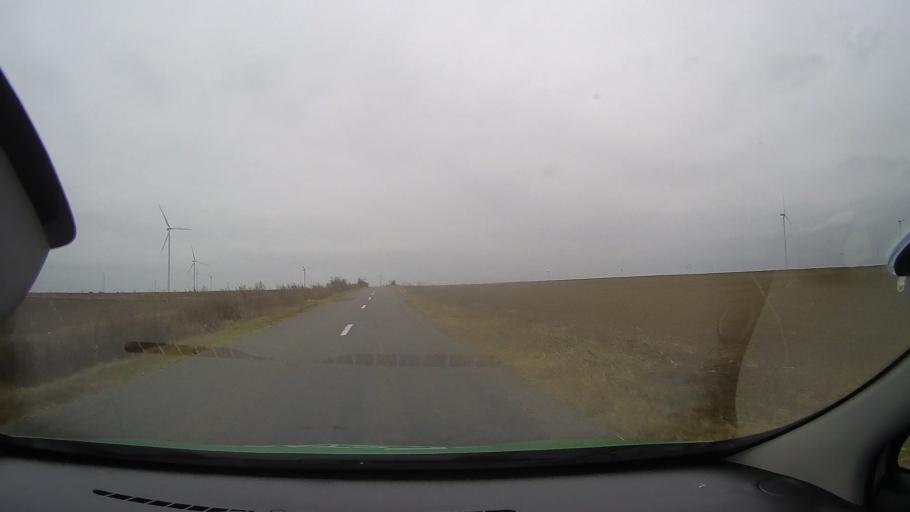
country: RO
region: Constanta
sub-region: Comuna Pantelimon
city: Pantelimon
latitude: 44.5077
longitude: 28.3434
